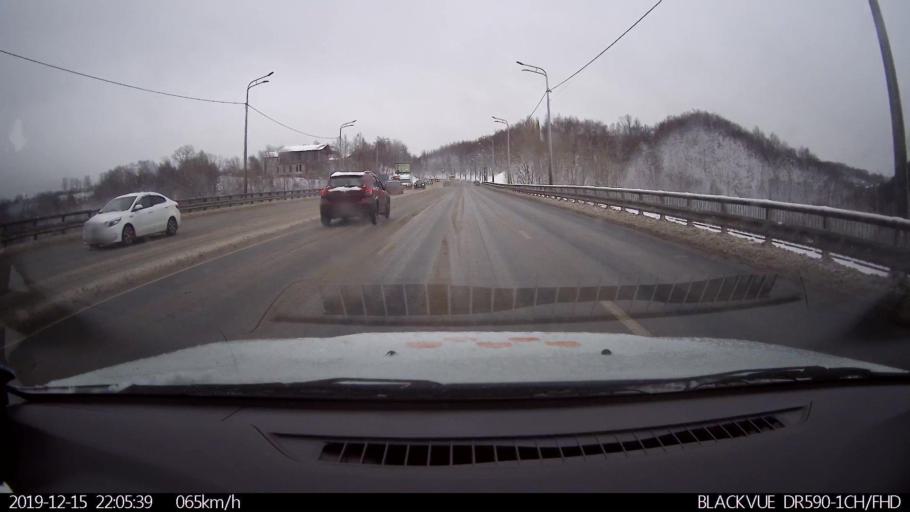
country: RU
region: Nizjnij Novgorod
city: Nizhniy Novgorod
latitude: 56.2481
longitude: 43.9514
